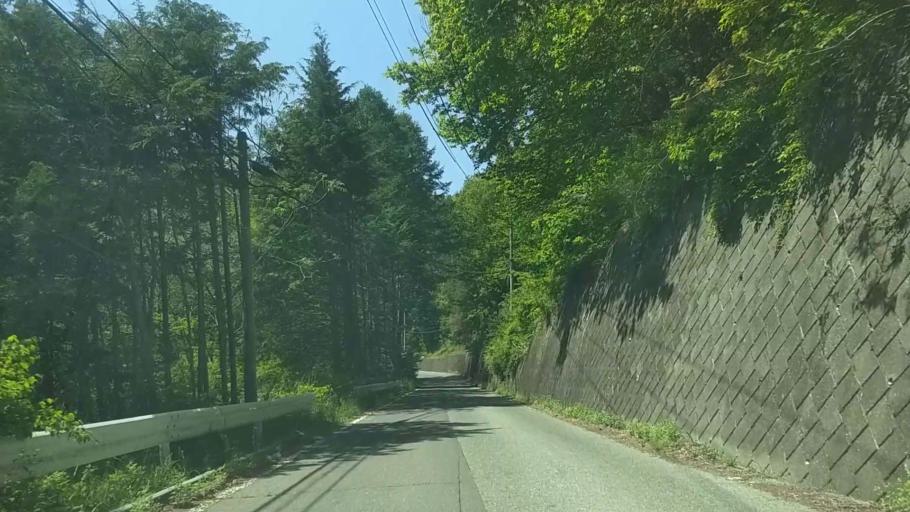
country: JP
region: Yamanashi
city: Nirasaki
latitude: 35.8911
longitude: 138.4536
